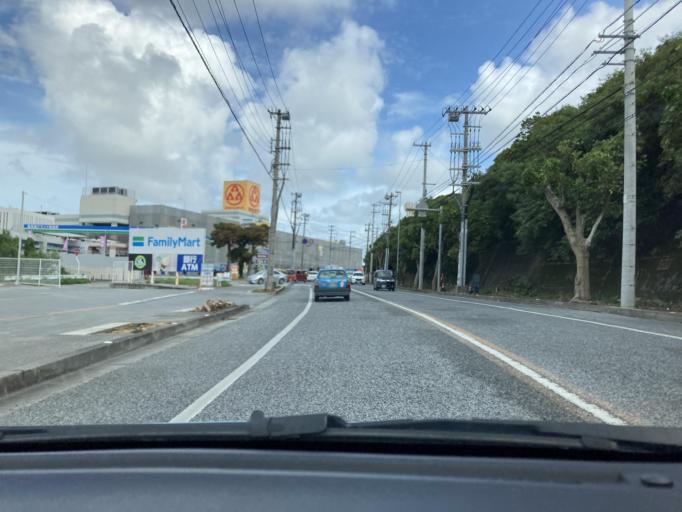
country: JP
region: Okinawa
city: Tomigusuku
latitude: 26.1749
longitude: 127.6869
